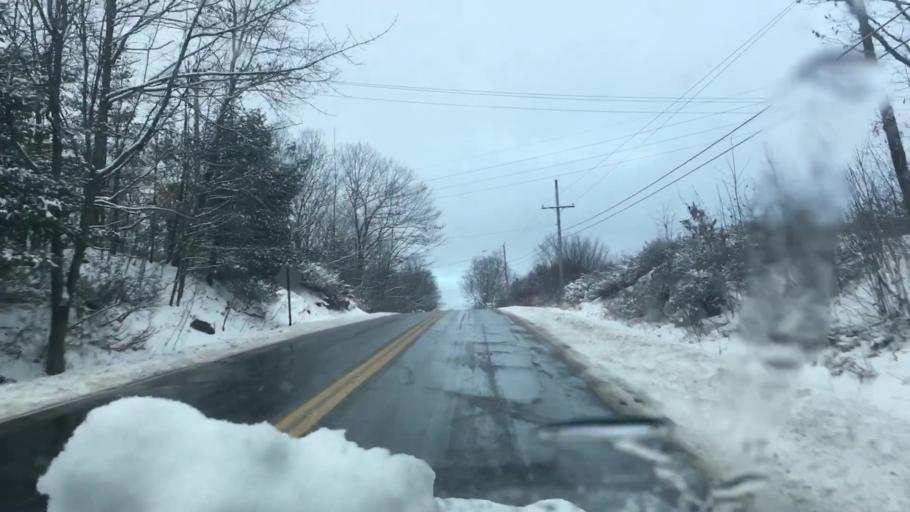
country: US
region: Maine
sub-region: Cumberland County
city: Westbrook
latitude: 43.6979
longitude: -70.3727
